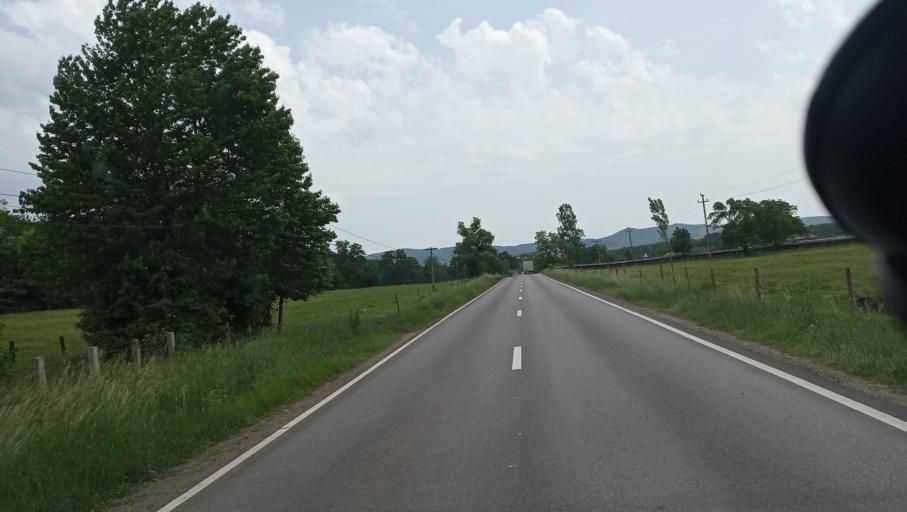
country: RO
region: Neamt
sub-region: Comuna Vanatori Neamt
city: Nemtisor
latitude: 47.2272
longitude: 26.2099
